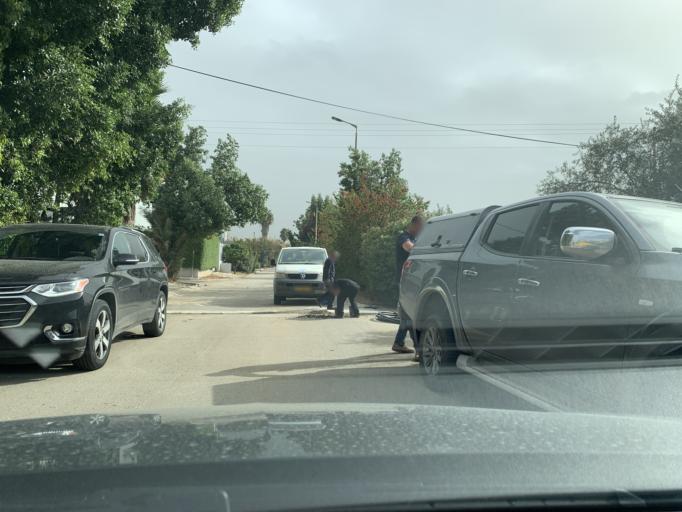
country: IL
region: Central District
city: Jaljulya
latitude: 32.1579
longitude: 34.9440
